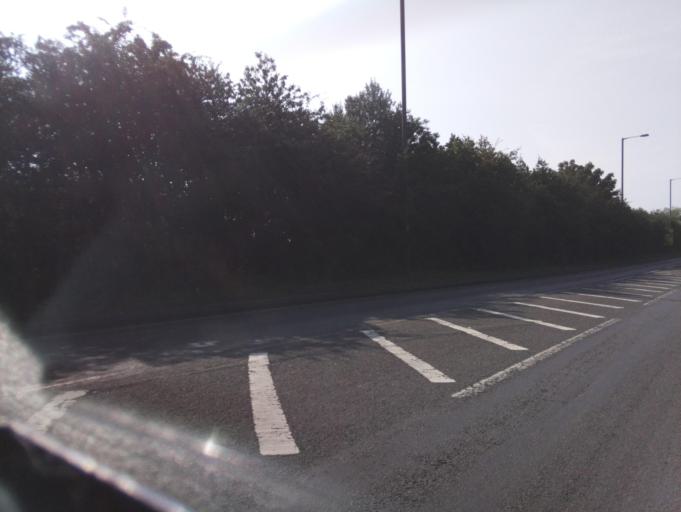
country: GB
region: England
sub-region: Walsall
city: Streetly
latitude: 52.6100
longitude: -1.8856
